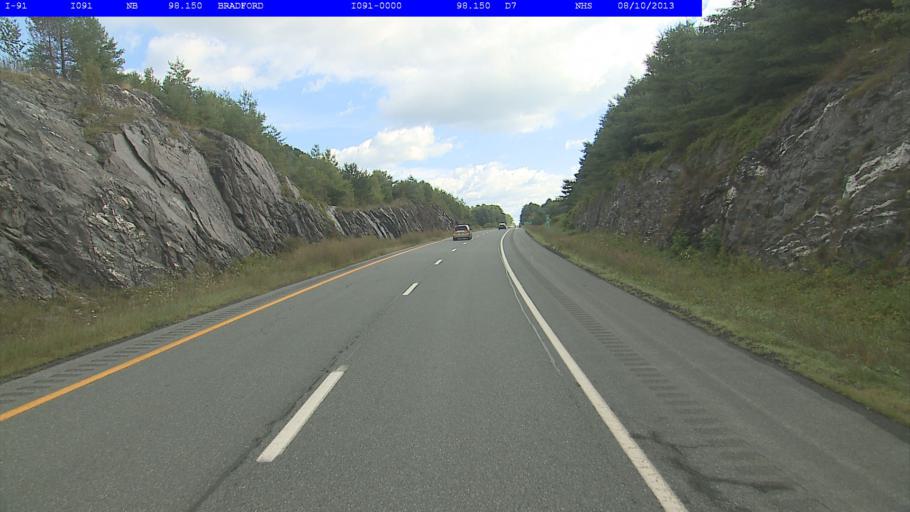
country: US
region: New Hampshire
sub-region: Grafton County
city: Haverhill
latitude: 43.9902
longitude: -72.1350
